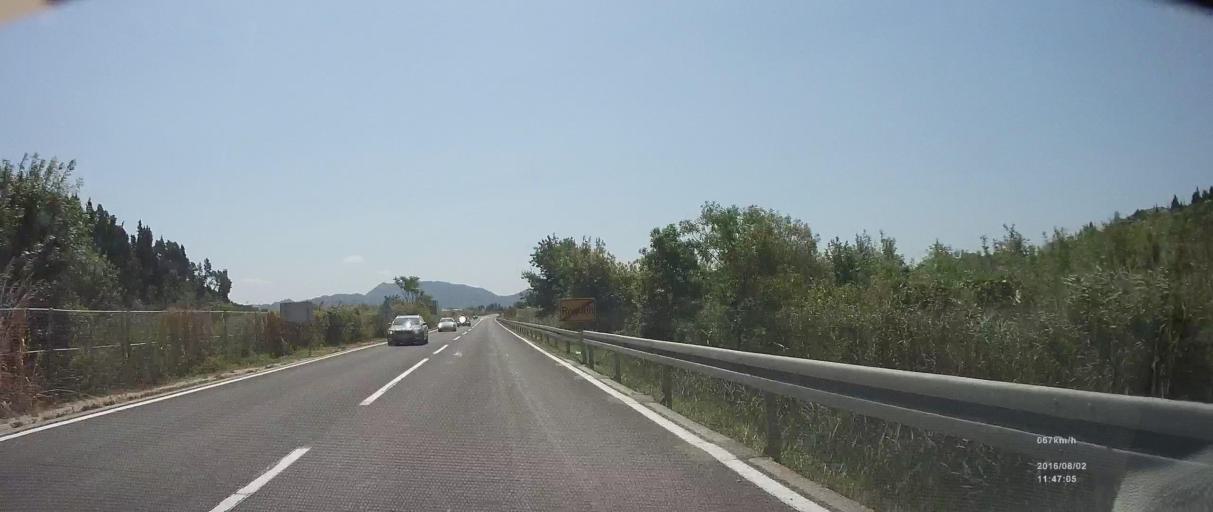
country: HR
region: Dubrovacko-Neretvanska
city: Komin
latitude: 43.0474
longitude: 17.4797
